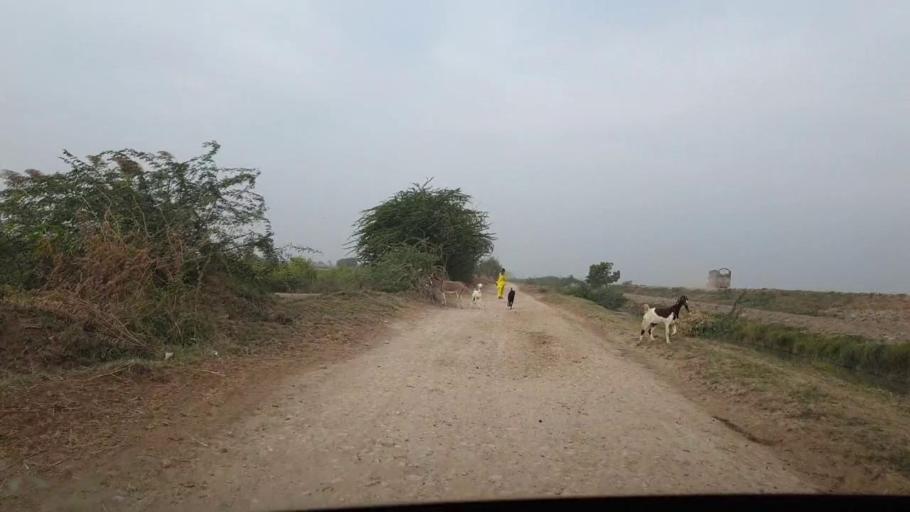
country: PK
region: Sindh
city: Chuhar Jamali
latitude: 24.4063
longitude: 67.9552
